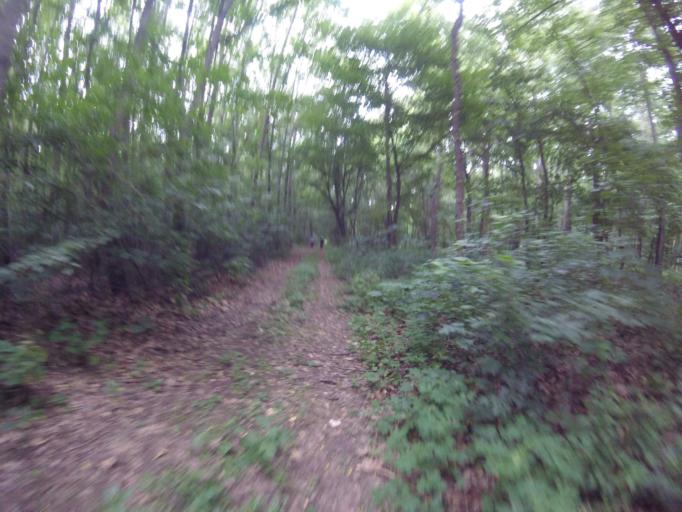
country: HU
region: Zala
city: Turje
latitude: 47.0092
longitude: 17.1427
